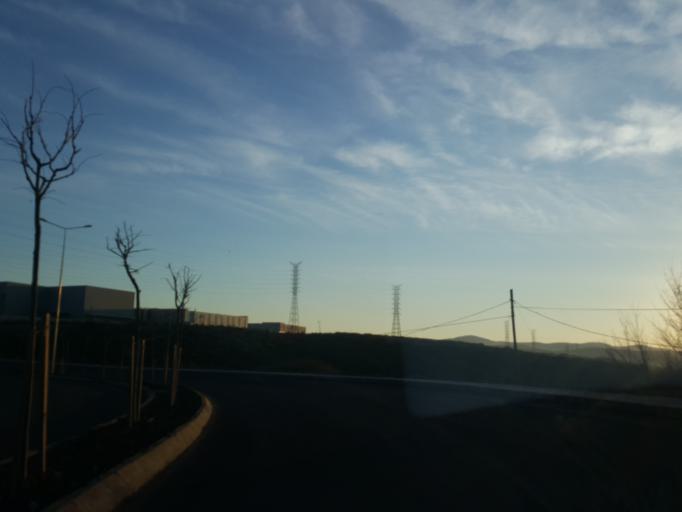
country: TR
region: Kocaeli
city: Tavsancil
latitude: 40.8066
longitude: 29.5581
